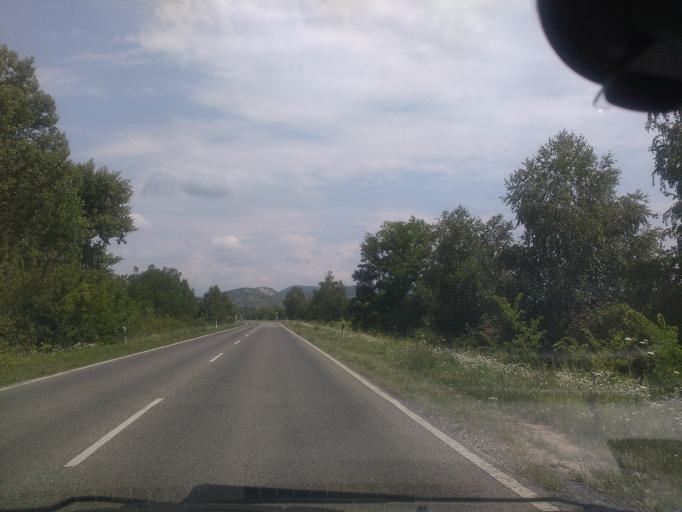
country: HU
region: Komarom-Esztergom
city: Dorog
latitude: 47.7513
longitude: 18.7146
